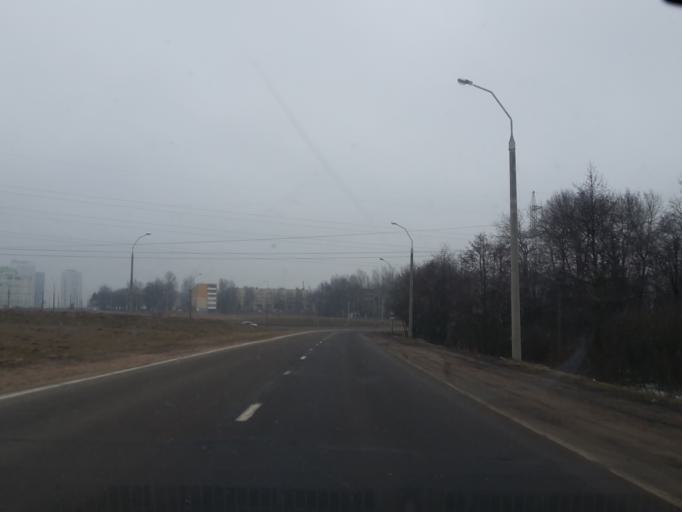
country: BY
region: Minsk
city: Zhdanovichy
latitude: 53.9109
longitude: 27.4059
